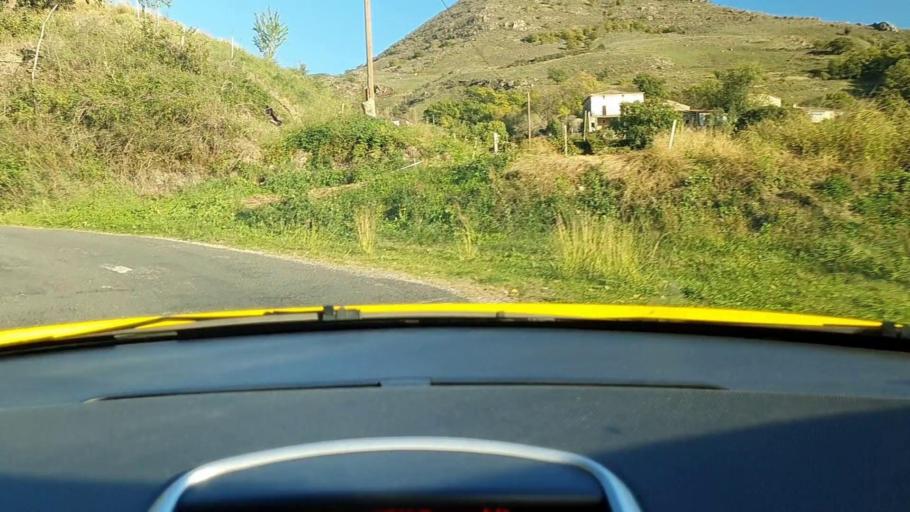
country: FR
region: Languedoc-Roussillon
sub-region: Departement du Gard
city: Sumene
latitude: 43.9822
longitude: 3.7428
